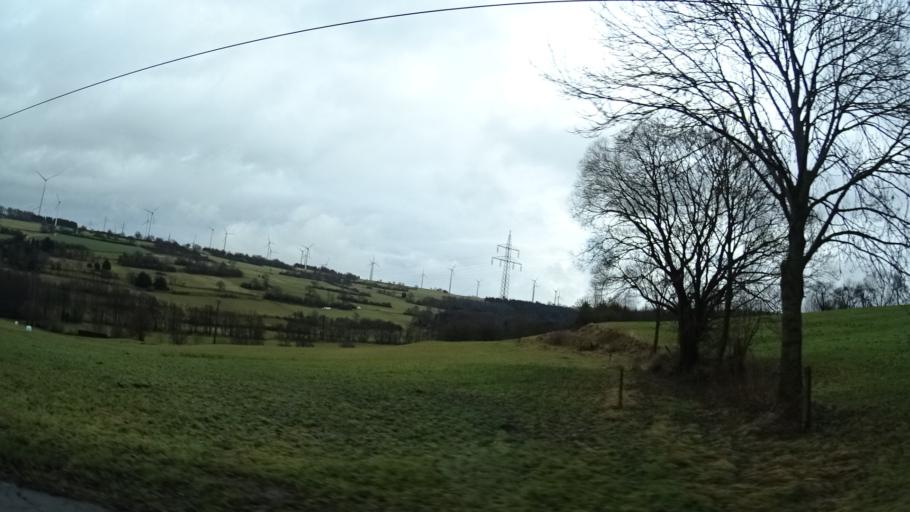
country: DE
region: Hesse
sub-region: Regierungsbezirk Giessen
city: Ulrichstein
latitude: 50.6021
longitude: 9.2250
